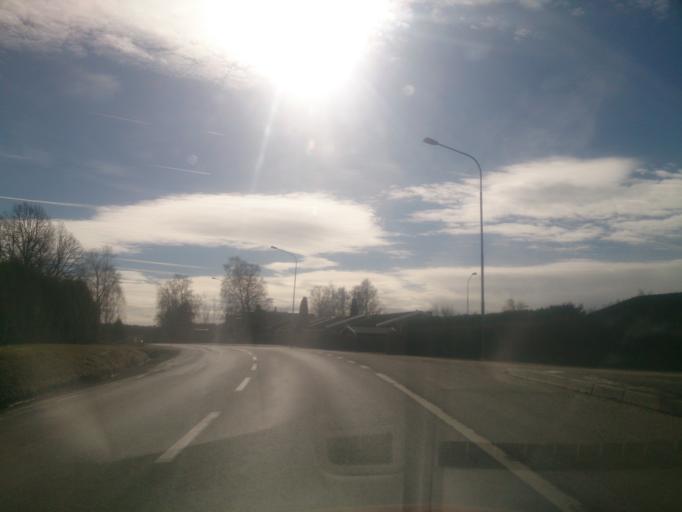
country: SE
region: OEstergoetland
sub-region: Finspangs Kommun
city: Finspang
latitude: 58.6874
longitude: 15.7505
